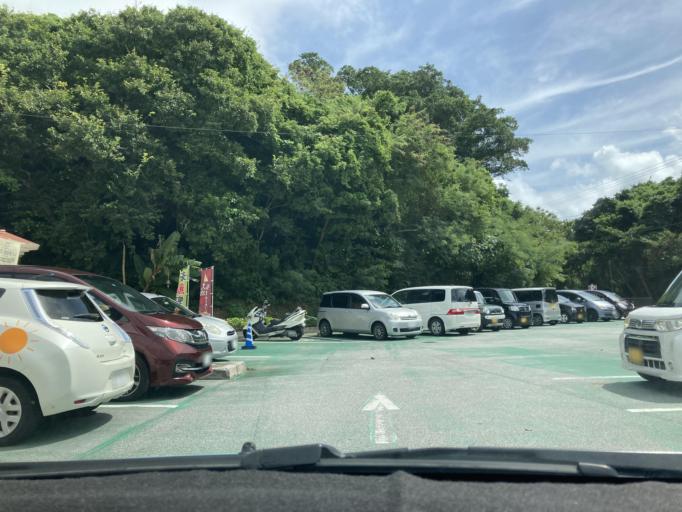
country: JP
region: Okinawa
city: Ginowan
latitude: 26.1690
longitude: 127.8271
